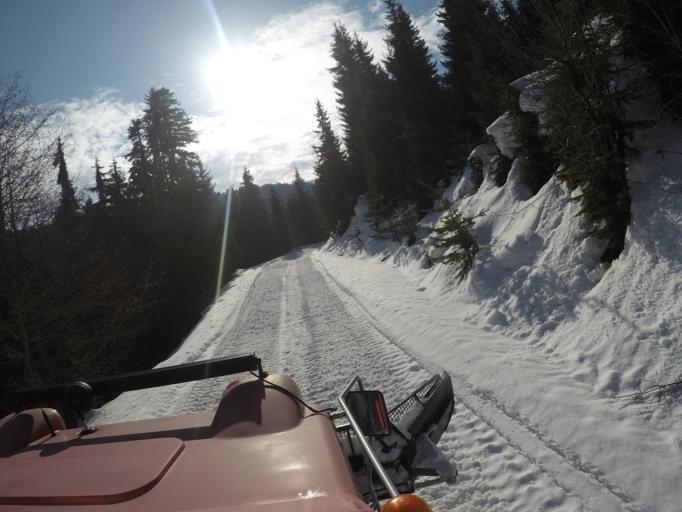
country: GE
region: Samtskhe-Javakheti
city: Adigeni
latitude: 41.6520
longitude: 42.6018
